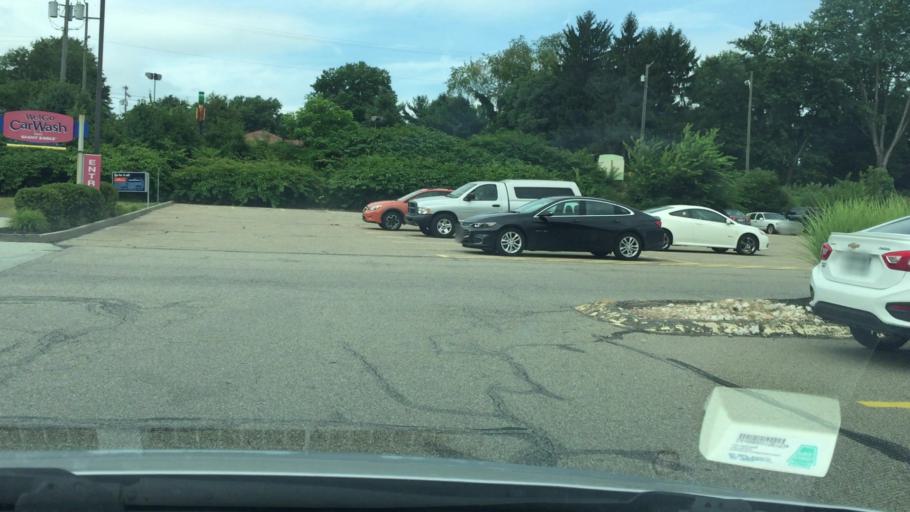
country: US
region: Pennsylvania
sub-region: Allegheny County
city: Tarentum
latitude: 40.5921
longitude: -79.7508
